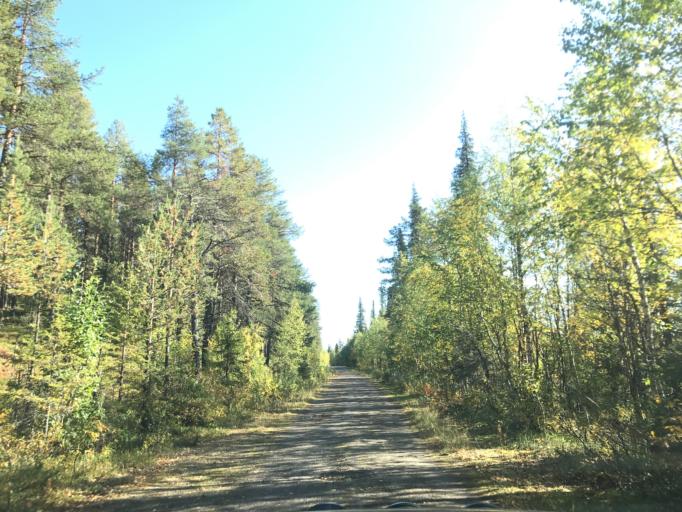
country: SE
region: Norrbotten
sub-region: Gallivare Kommun
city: Malmberget
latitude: 67.6470
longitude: 21.0924
